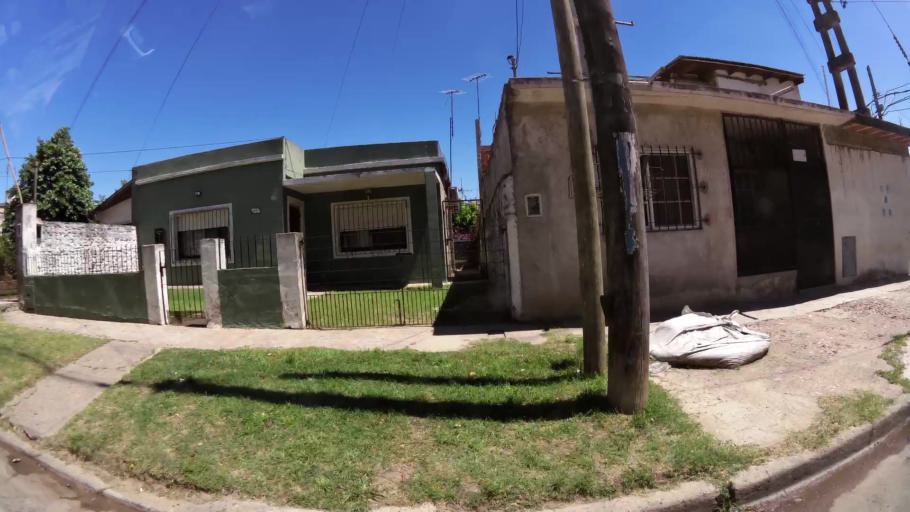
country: AR
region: Buenos Aires
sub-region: Partido de Tigre
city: Tigre
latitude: -34.5051
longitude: -58.5855
